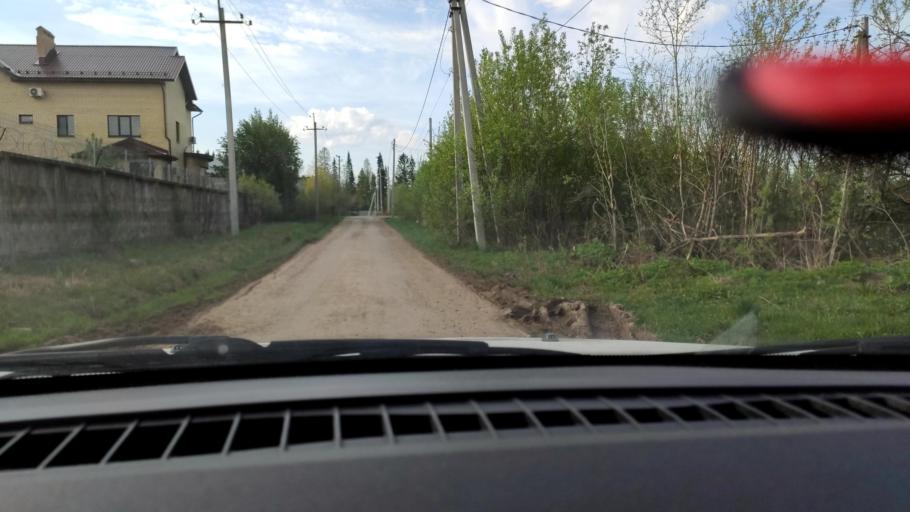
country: RU
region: Perm
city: Froly
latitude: 57.9517
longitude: 56.2849
